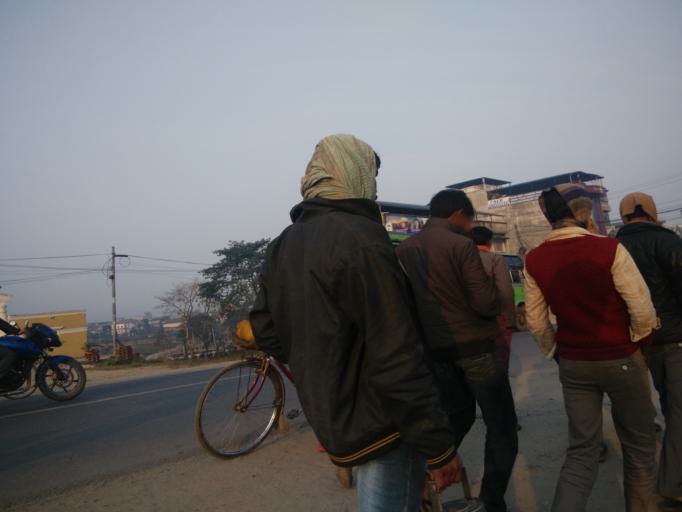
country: NP
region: Central Region
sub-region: Narayani Zone
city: Bharatpur
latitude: 27.6902
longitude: 84.4267
